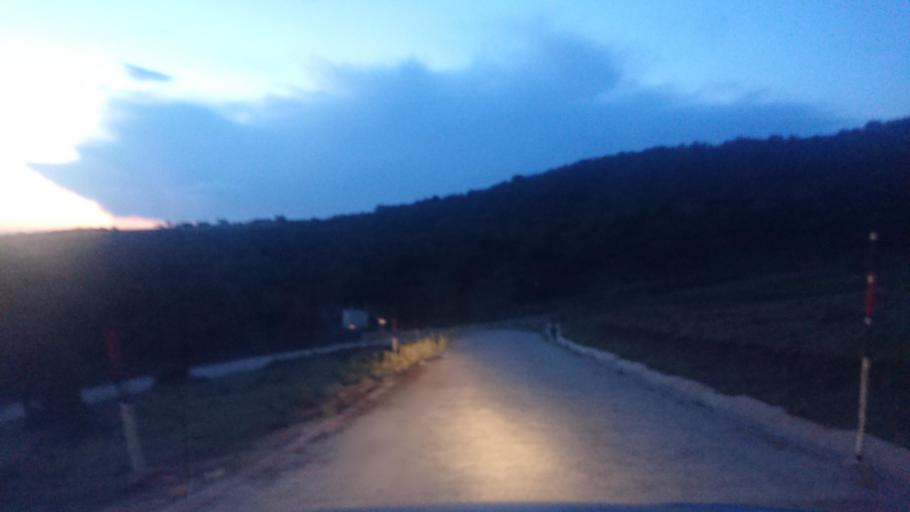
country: TR
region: Aksaray
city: Ortakoy
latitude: 38.6432
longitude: 34.0236
